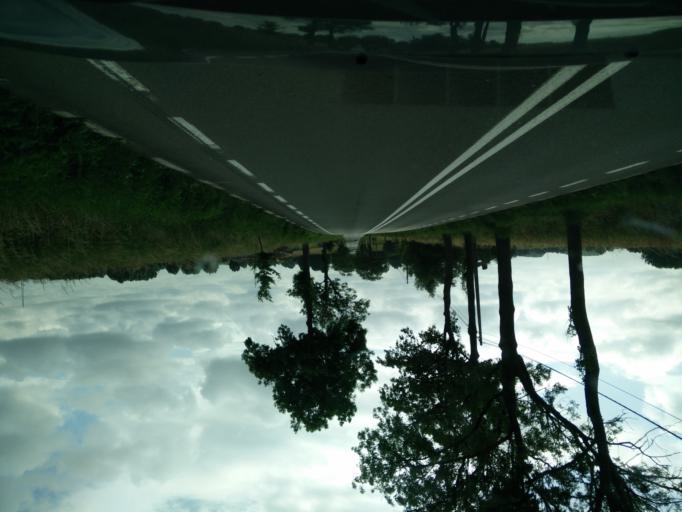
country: BE
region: Wallonia
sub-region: Province du Hainaut
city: Flobecq
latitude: 50.7304
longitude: 3.7535
